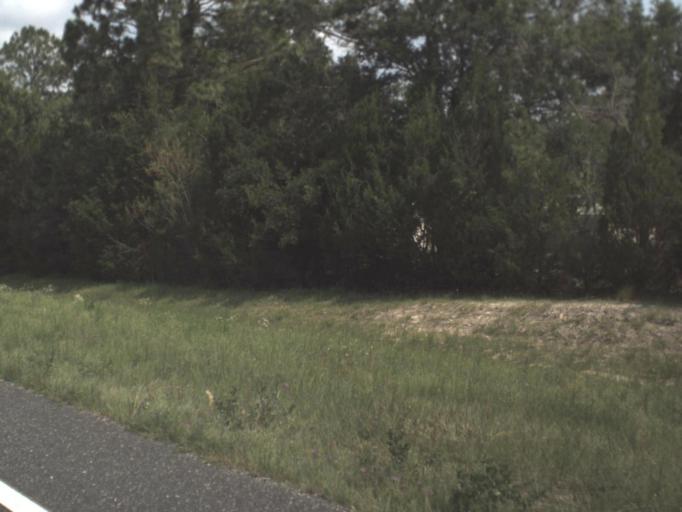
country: US
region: Florida
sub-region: Levy County
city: Bronson
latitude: 29.4379
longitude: -82.6198
